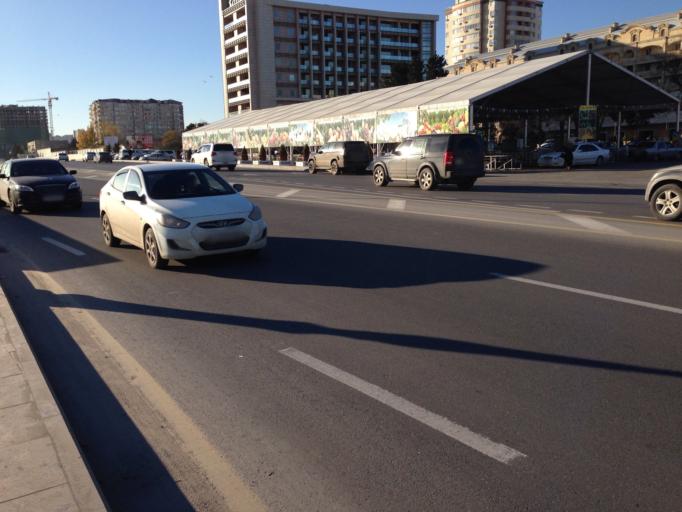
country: AZ
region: Baki
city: Baku
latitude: 40.4002
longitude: 49.8506
